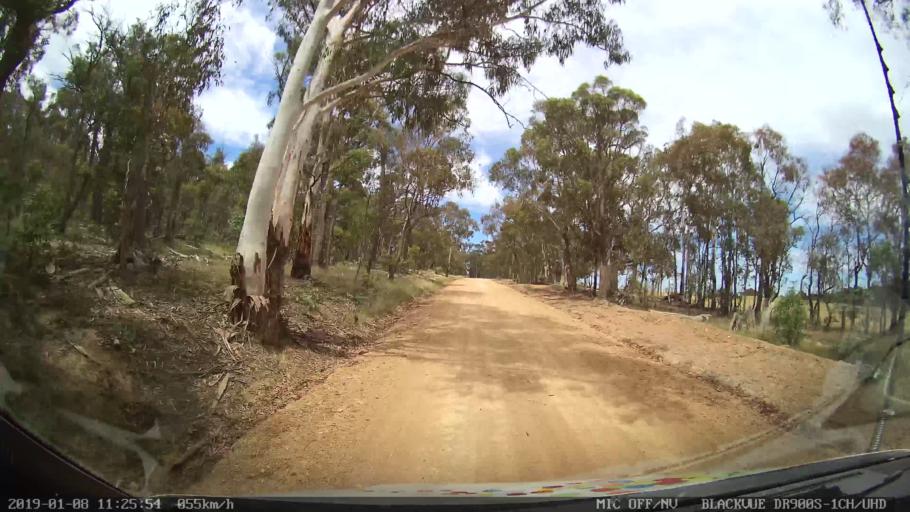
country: AU
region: New South Wales
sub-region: Guyra
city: Guyra
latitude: -30.2766
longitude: 151.5600
